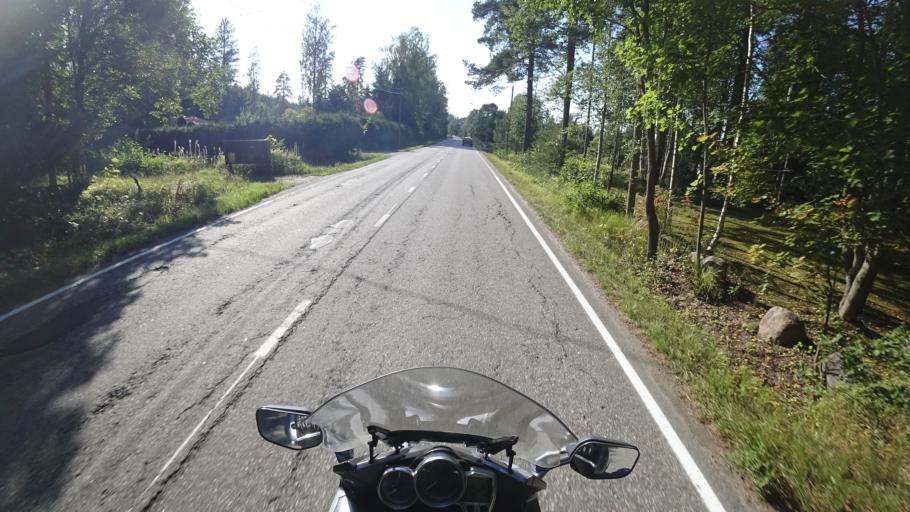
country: FI
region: Uusimaa
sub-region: Helsinki
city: Sammatti
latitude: 60.3172
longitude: 23.8399
